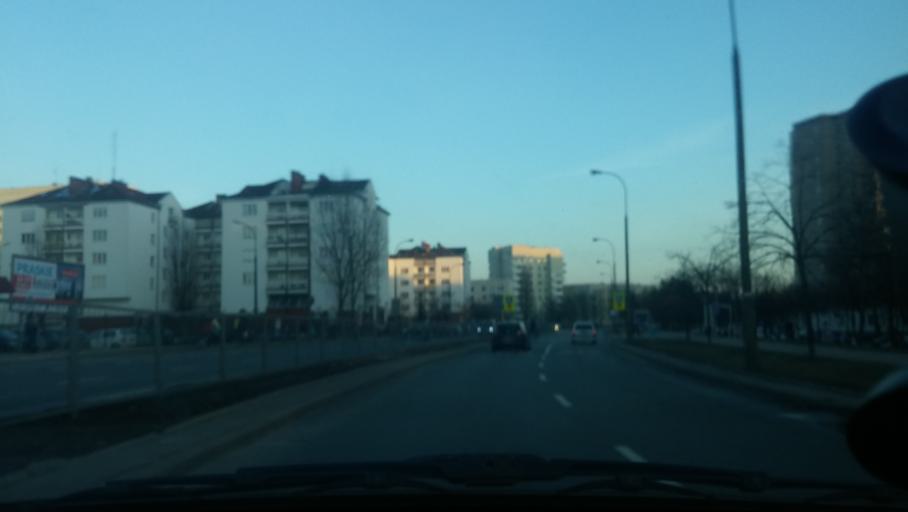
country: PL
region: Masovian Voivodeship
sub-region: Warszawa
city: Praga Poludnie
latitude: 52.2263
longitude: 21.0999
